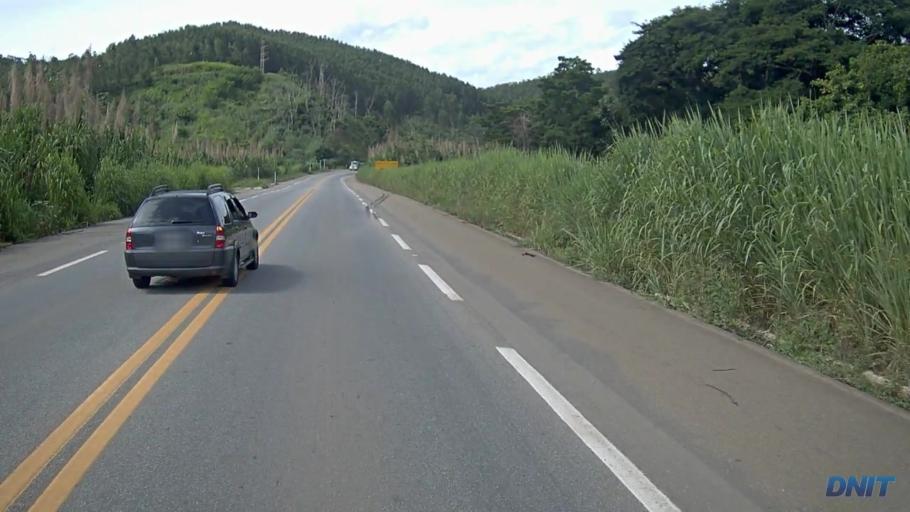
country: BR
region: Minas Gerais
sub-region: Ipaba
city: Ipaba
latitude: -19.3633
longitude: -42.4485
